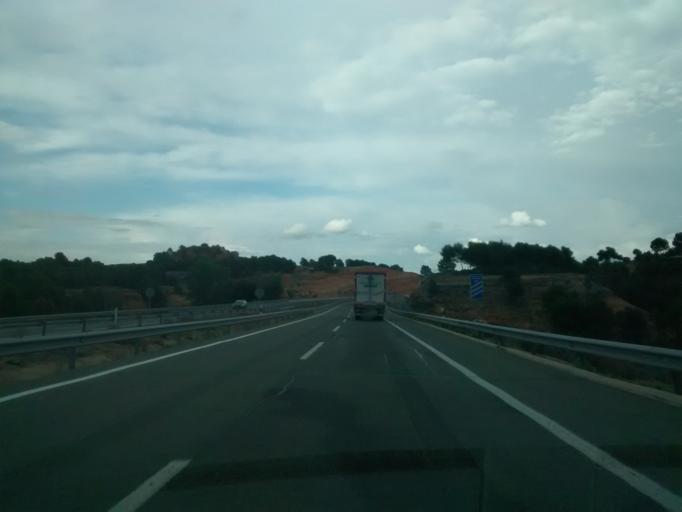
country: ES
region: Aragon
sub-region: Provincia de Zaragoza
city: Ariza
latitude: 41.3173
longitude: -2.0623
